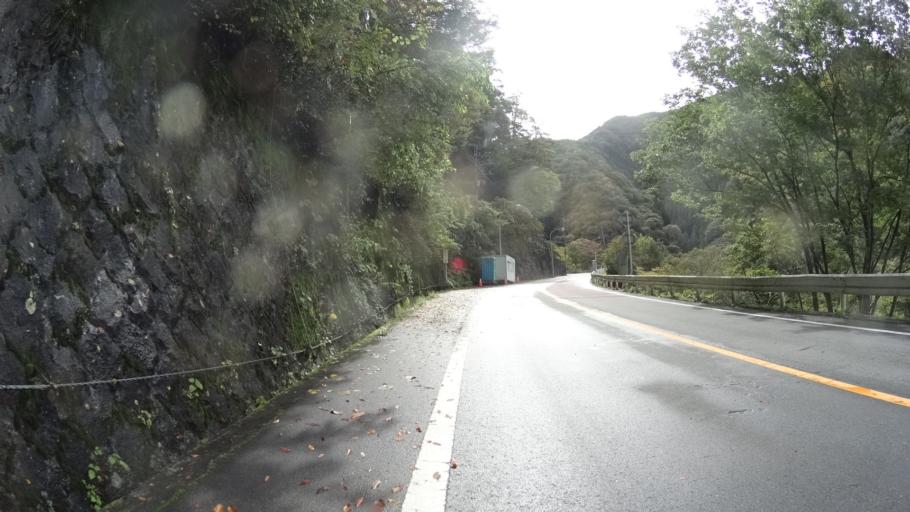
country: JP
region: Yamanashi
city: Otsuki
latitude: 35.7874
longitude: 138.9654
